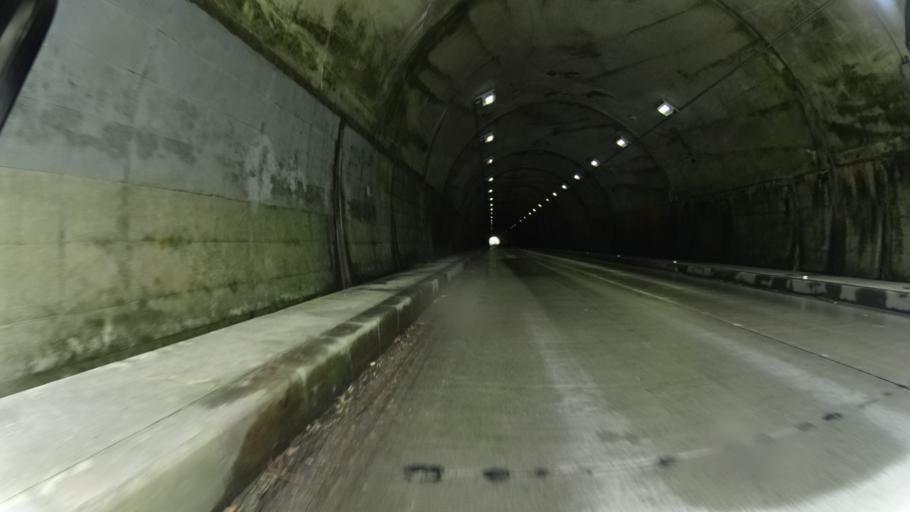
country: JP
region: Tokyo
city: Ome
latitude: 35.8315
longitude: 139.2117
